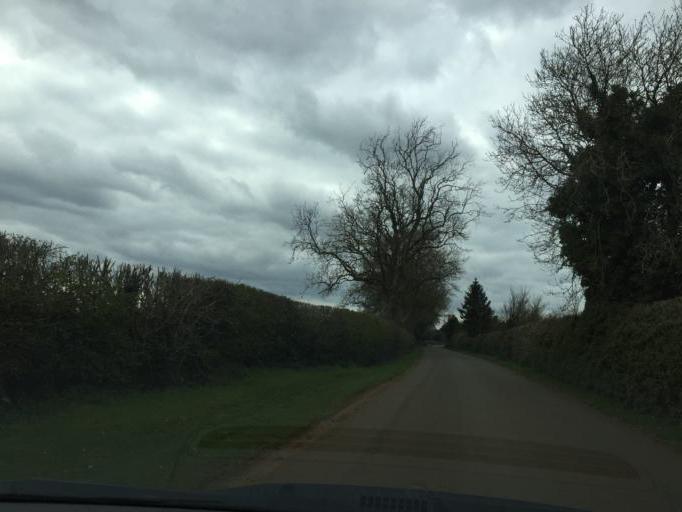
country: GB
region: England
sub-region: Oxfordshire
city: Hanwell
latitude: 52.1083
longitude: -1.4385
